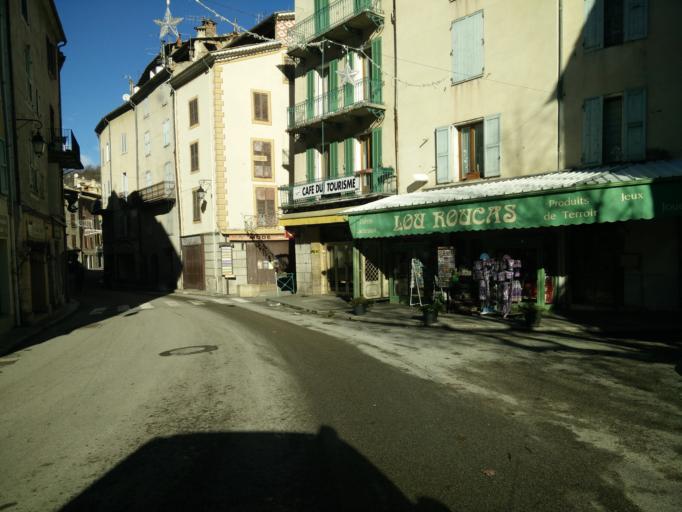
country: FR
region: Provence-Alpes-Cote d'Azur
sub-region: Departement des Alpes-de-Haute-Provence
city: Castellane
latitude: 43.8465
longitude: 6.5126
